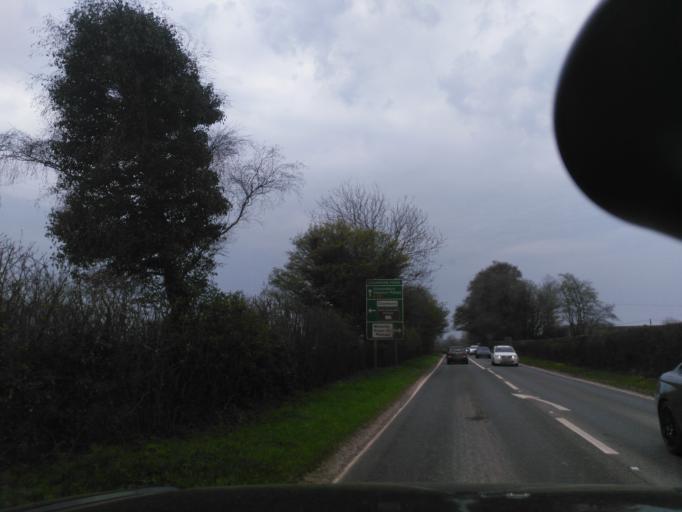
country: GB
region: England
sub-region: Somerset
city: Evercreech
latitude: 51.1901
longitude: -2.4796
